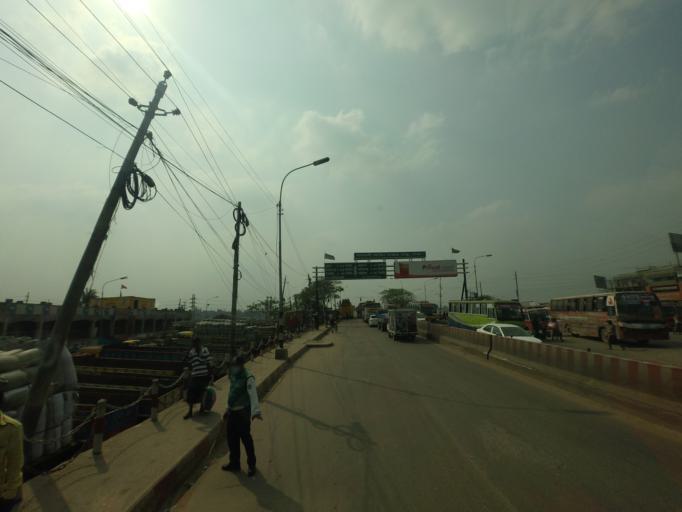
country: BD
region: Dhaka
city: Azimpur
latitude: 23.7833
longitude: 90.3378
